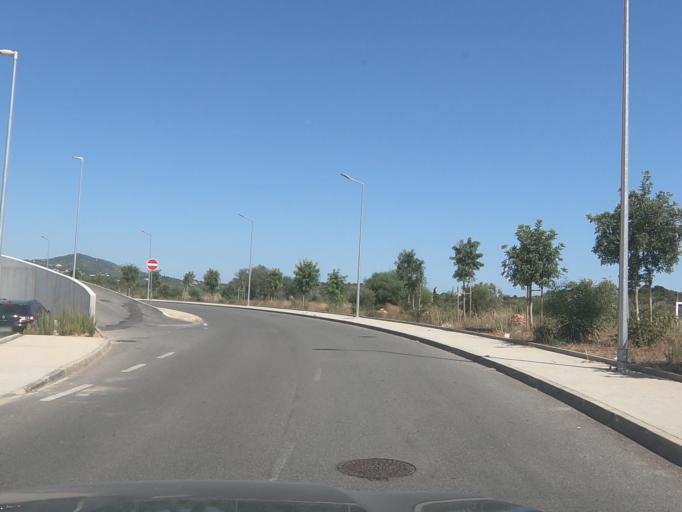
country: PT
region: Faro
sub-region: Faro
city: Santa Barbara de Nexe
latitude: 37.0963
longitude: -7.9964
